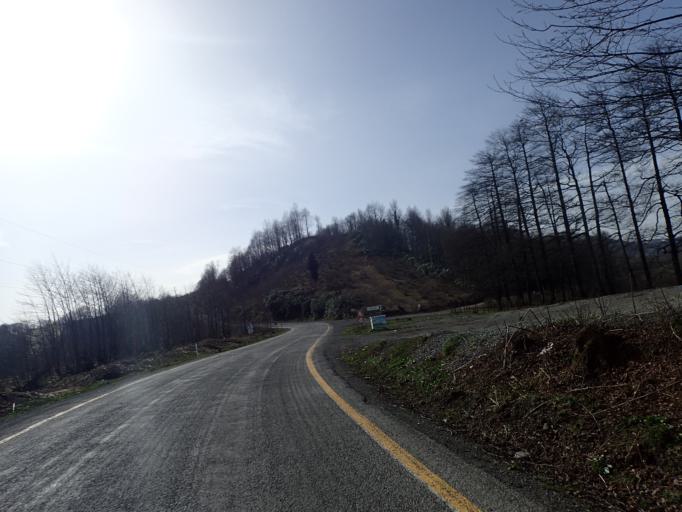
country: TR
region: Ordu
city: Kabaduz
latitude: 40.7779
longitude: 37.9243
